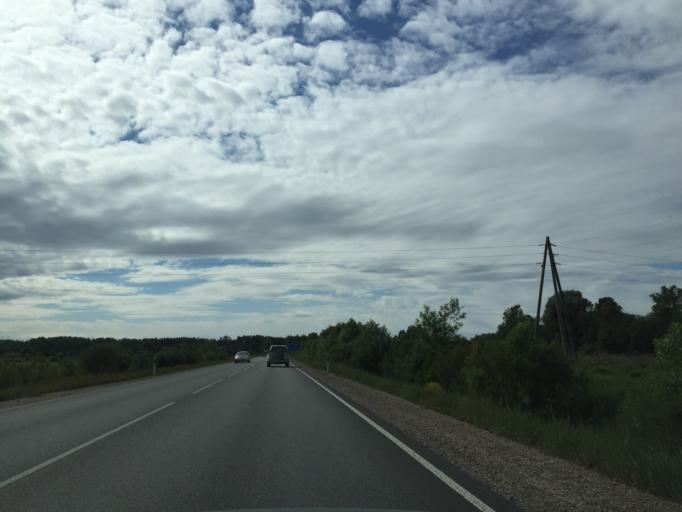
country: LV
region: Salaspils
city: Salaspils
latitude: 56.8997
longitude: 24.4161
